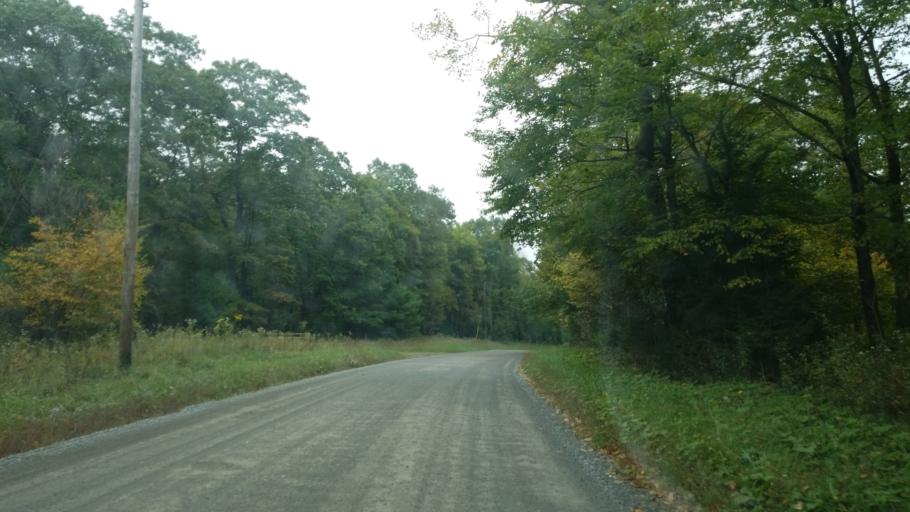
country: US
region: Pennsylvania
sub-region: Clearfield County
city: Curwensville
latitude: 41.0428
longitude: -78.5703
